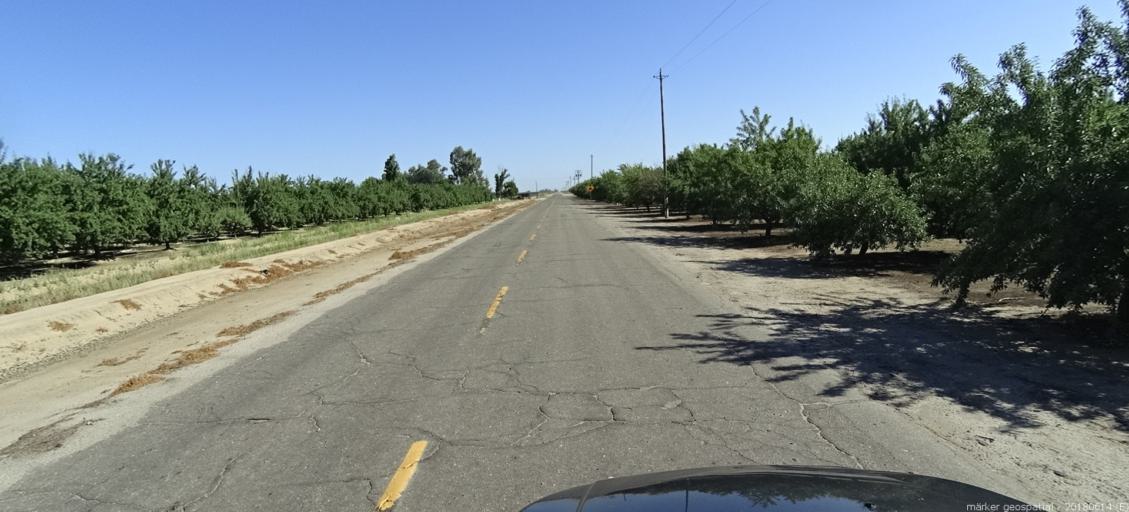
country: US
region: California
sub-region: Madera County
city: Fairmead
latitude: 36.9941
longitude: -120.1661
